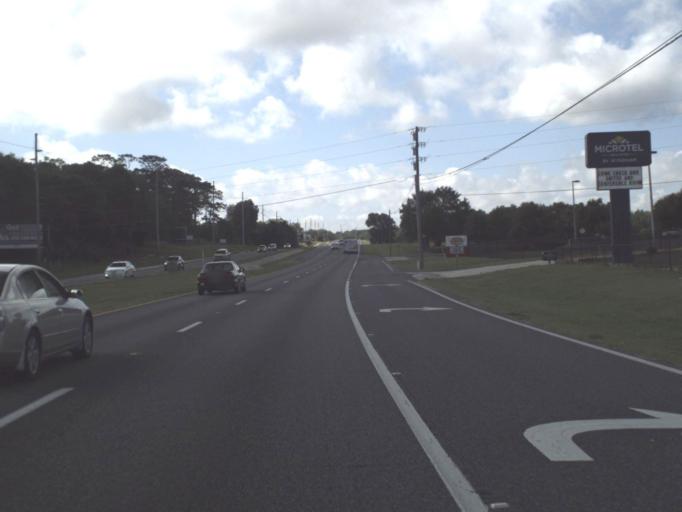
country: US
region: Florida
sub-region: Lake County
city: Lady Lake
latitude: 28.8988
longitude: -81.9110
